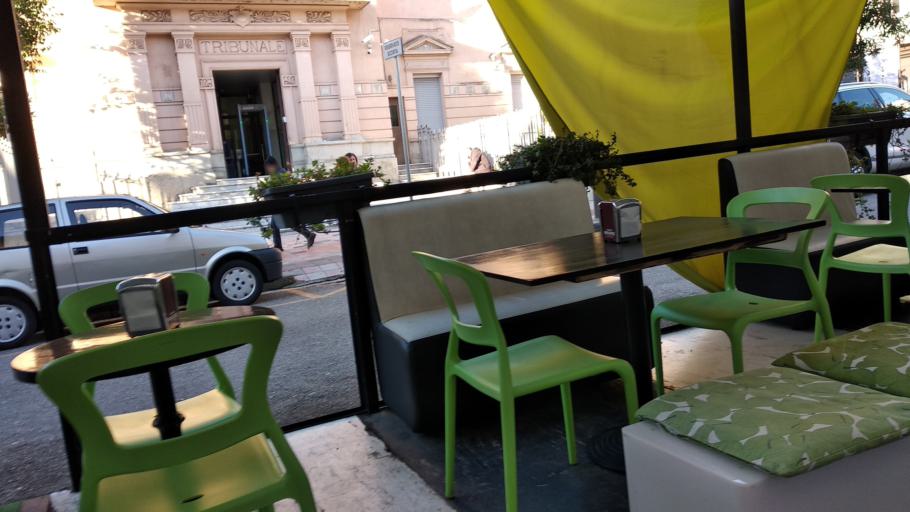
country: IT
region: Calabria
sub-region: Provincia di Reggio Calabria
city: Seminara
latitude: 38.3579
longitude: 15.8486
